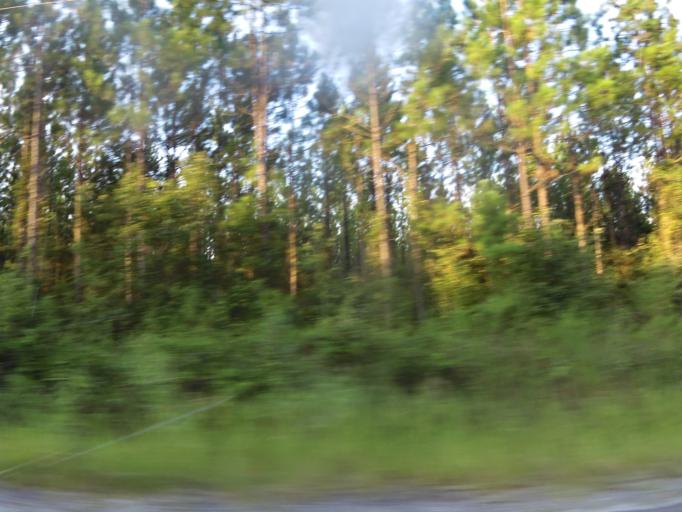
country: US
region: Florida
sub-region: Duval County
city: Baldwin
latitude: 30.3871
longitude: -82.0480
